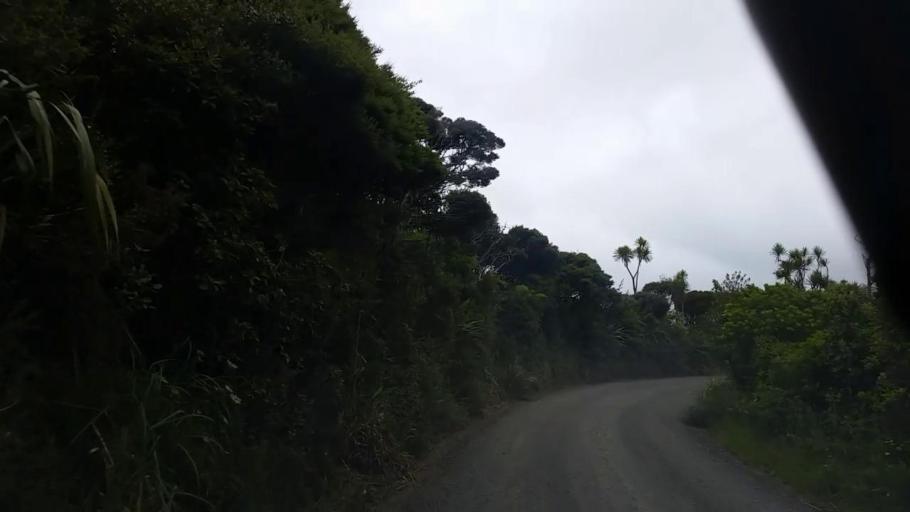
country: NZ
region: Auckland
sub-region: Auckland
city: Muriwai Beach
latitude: -36.9294
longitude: 174.4679
